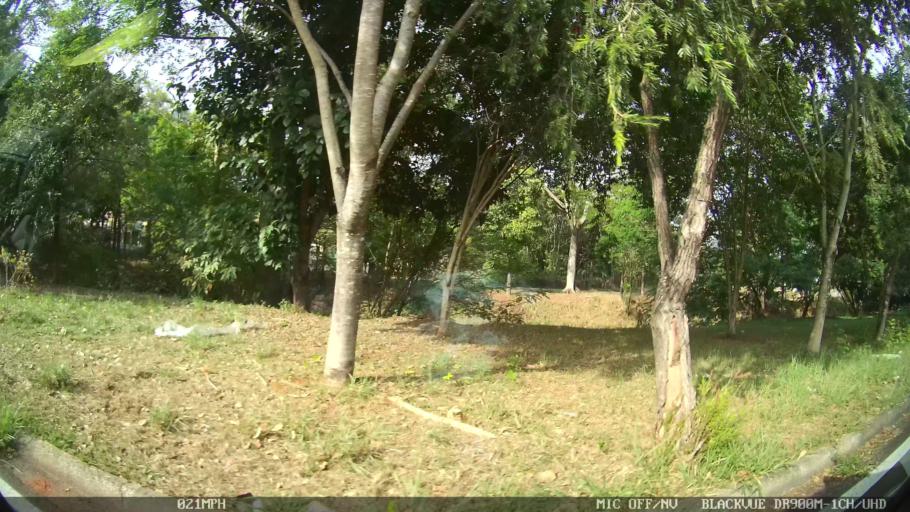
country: BR
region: Sao Paulo
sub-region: Piracicaba
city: Piracicaba
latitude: -22.7204
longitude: -47.6249
